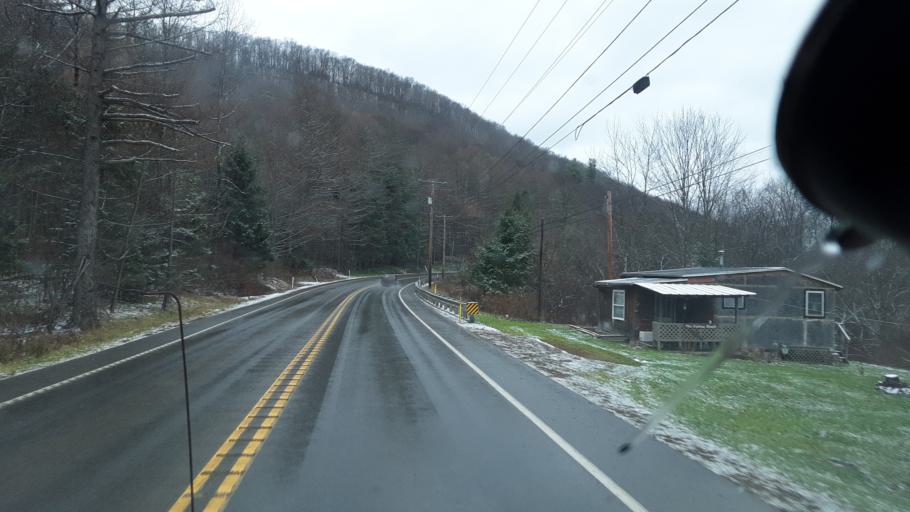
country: US
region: Pennsylvania
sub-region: Potter County
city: Shinglehouse
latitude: 41.9024
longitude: -78.0829
